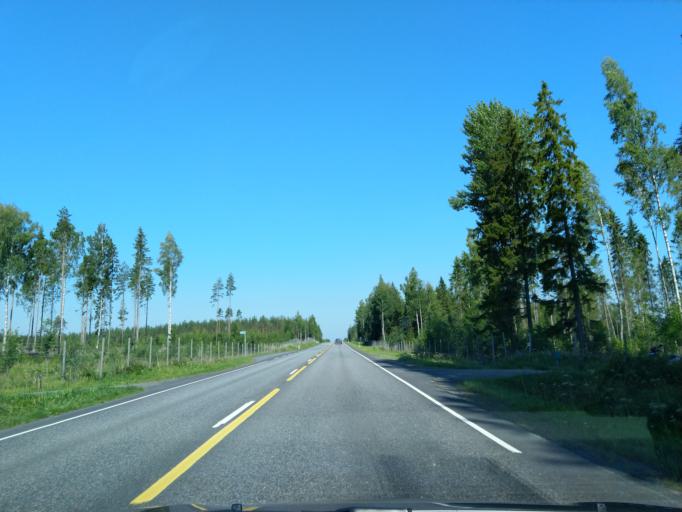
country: FI
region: Pirkanmaa
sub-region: Lounais-Pirkanmaa
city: Punkalaidun
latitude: 61.0187
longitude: 23.0589
